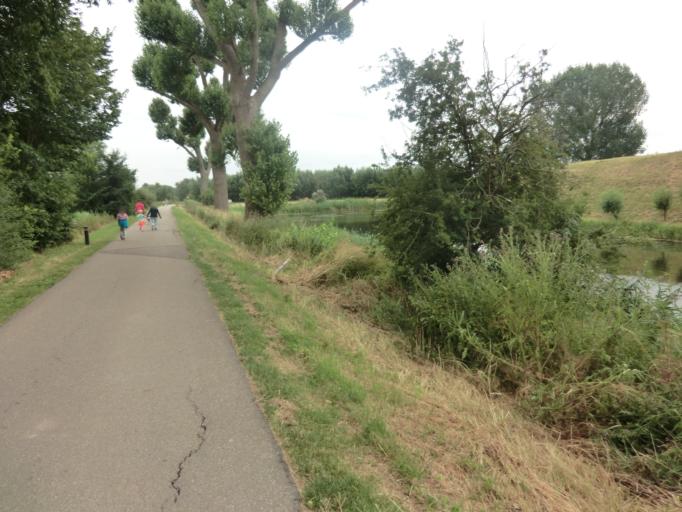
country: NL
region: North Brabant
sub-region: Gemeente Woudrichem
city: Woudrichem
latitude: 51.8168
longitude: 5.0233
